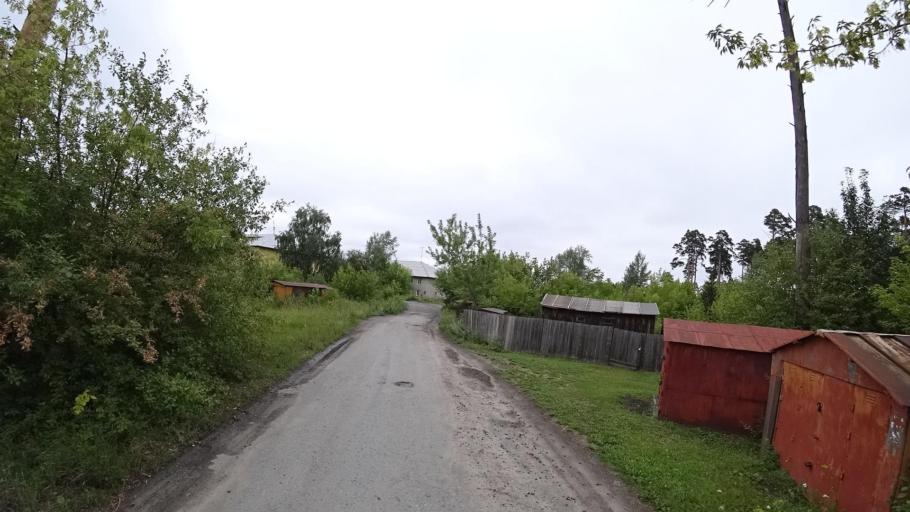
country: RU
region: Sverdlovsk
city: Kamyshlov
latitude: 56.8408
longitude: 62.7430
